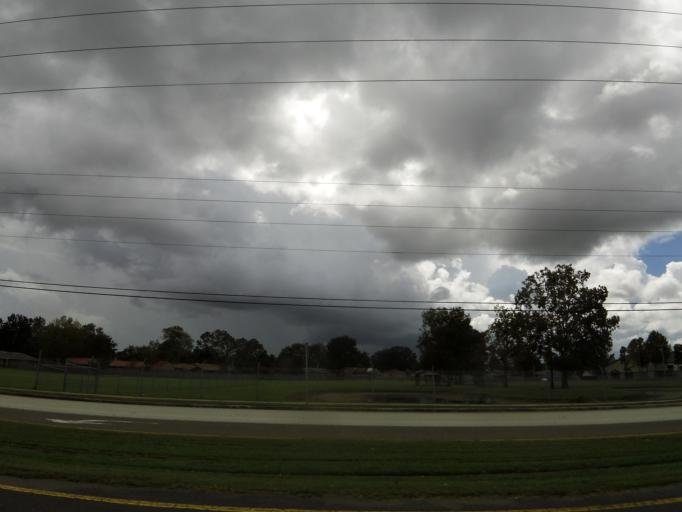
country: US
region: Florida
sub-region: Clay County
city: Lakeside
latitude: 30.1007
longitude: -81.7549
